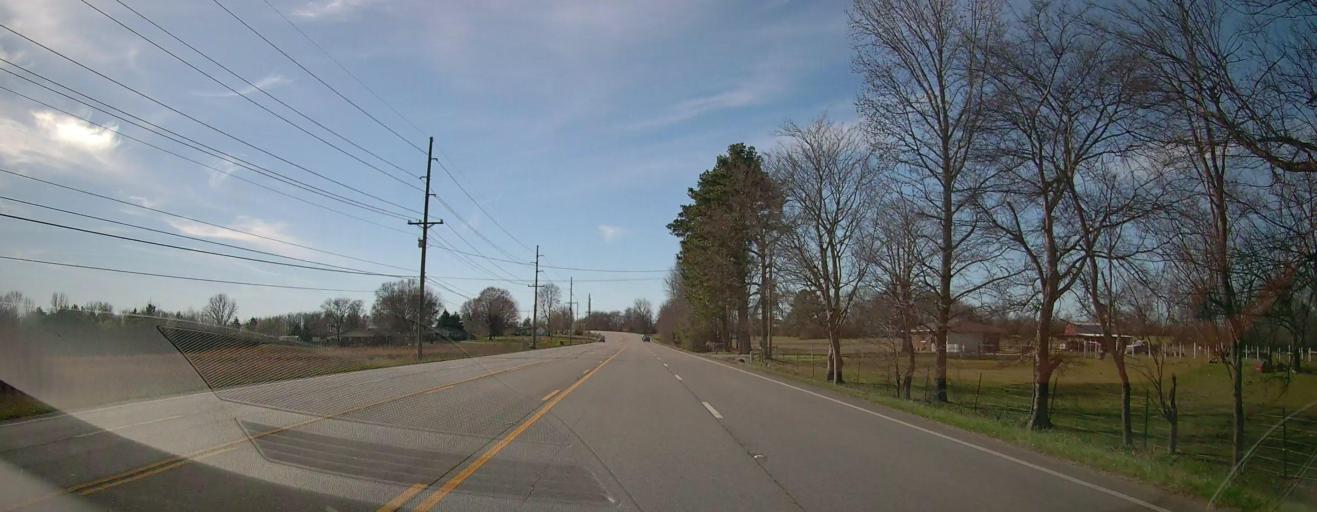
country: US
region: Alabama
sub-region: Limestone County
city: Athens
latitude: 34.7939
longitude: -87.1080
